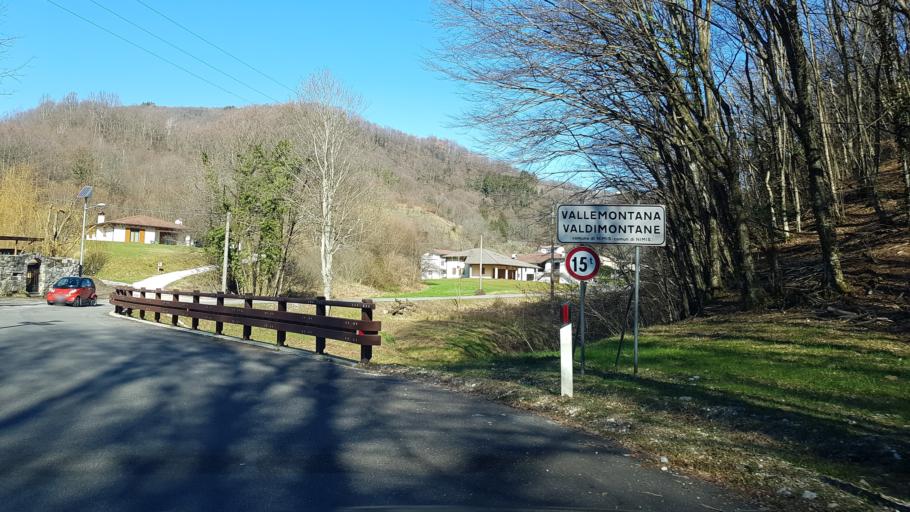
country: IT
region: Friuli Venezia Giulia
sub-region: Provincia di Udine
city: Nimis
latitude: 46.2138
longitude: 13.2928
